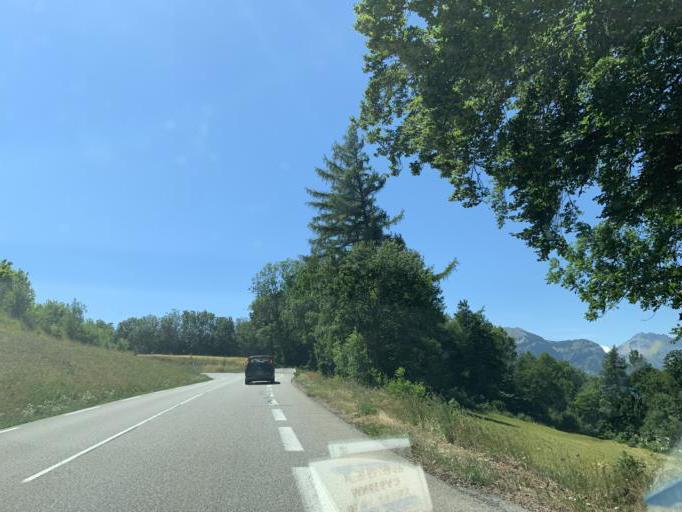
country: FR
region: Provence-Alpes-Cote d'Azur
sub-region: Departement des Hautes-Alpes
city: Saint-Bonnet-en-Champsaur
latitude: 44.6330
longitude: 6.1310
